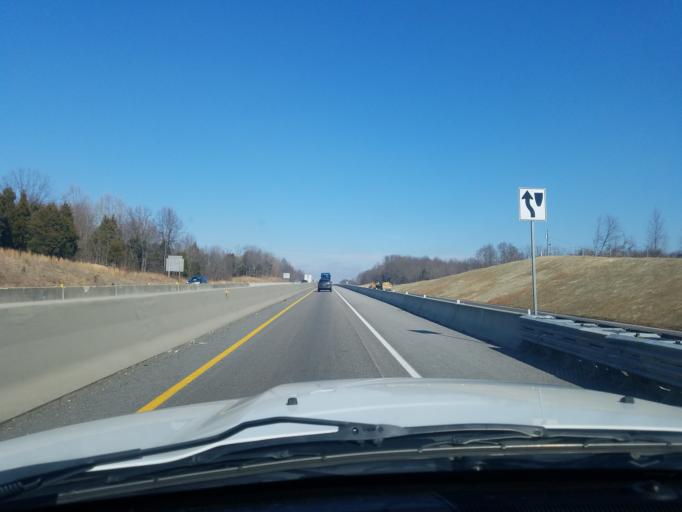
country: US
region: Kentucky
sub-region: Hardin County
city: Elizabethtown
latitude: 37.6018
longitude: -85.8674
